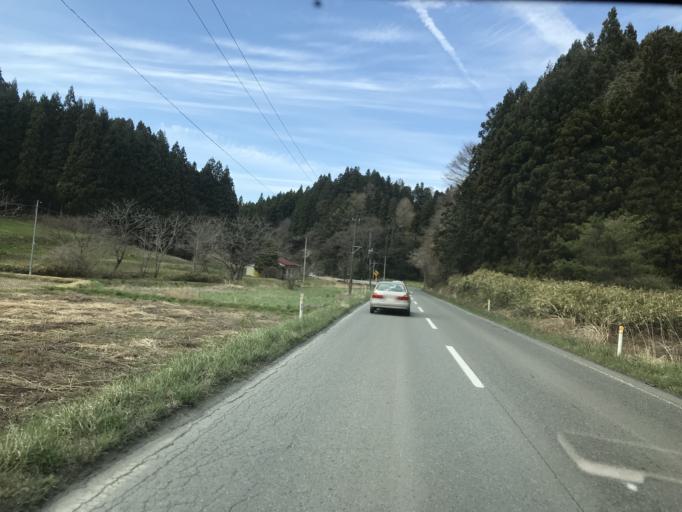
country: JP
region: Iwate
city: Ichinoseki
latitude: 38.8370
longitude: 141.3420
